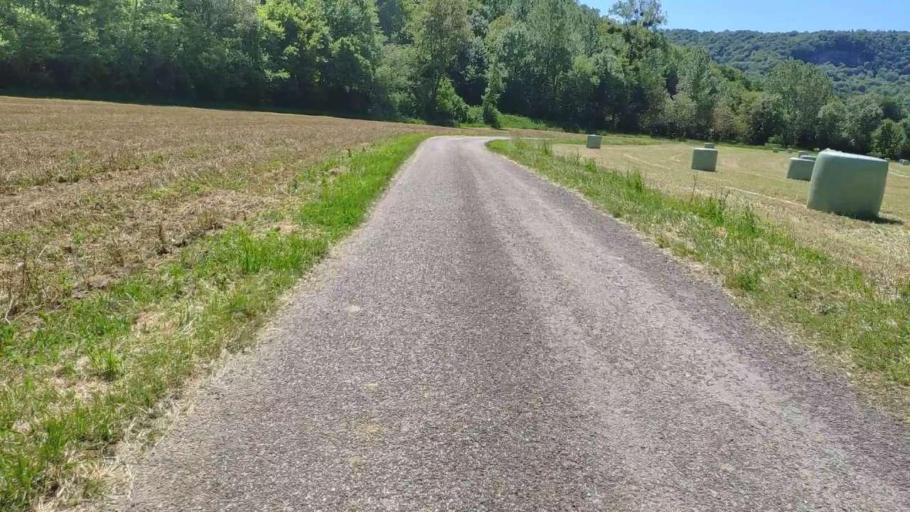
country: FR
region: Franche-Comte
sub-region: Departement du Jura
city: Perrigny
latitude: 46.7344
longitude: 5.6462
